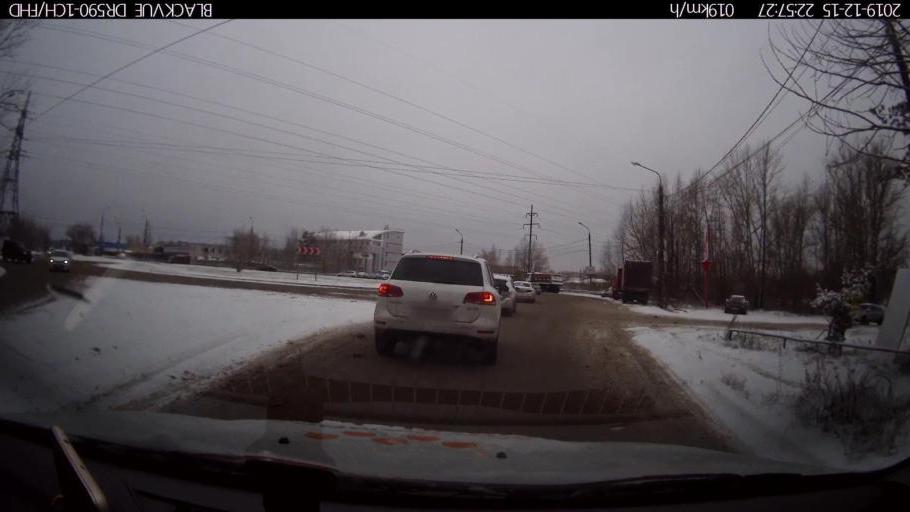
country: RU
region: Nizjnij Novgorod
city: Neklyudovo
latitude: 56.3452
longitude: 43.8896
